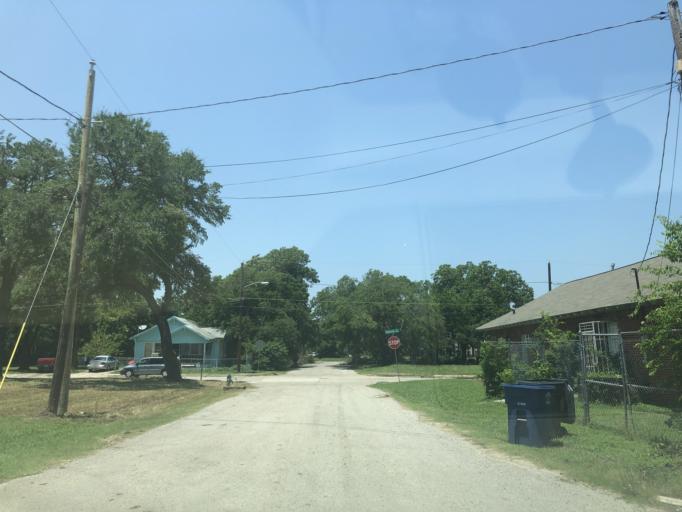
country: US
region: Texas
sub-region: Dallas County
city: Dallas
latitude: 32.7745
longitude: -96.8398
